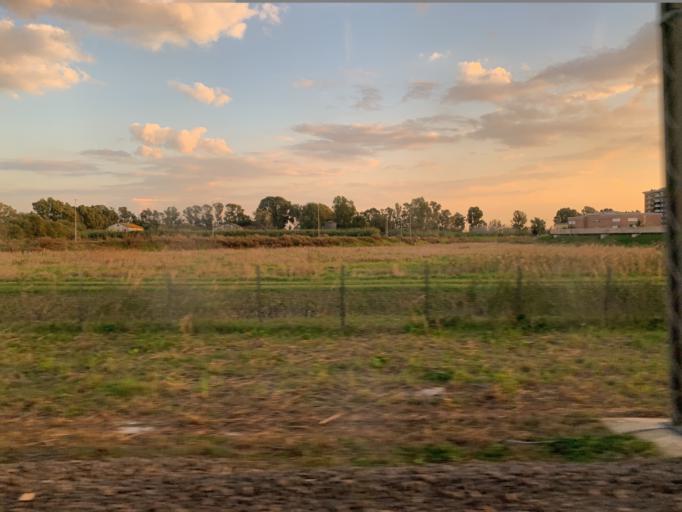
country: IT
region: Latium
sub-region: Citta metropolitana di Roma Capitale
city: Npp 23 (Parco Leonardo)
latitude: 41.8061
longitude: 12.3102
